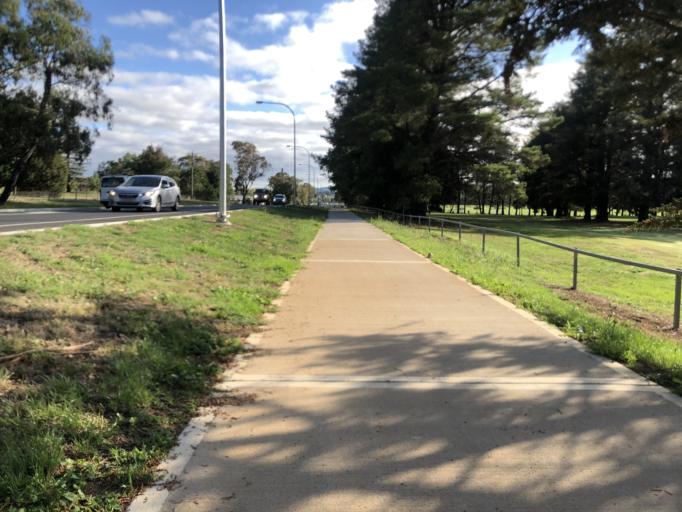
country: AU
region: New South Wales
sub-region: Orange Municipality
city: Orange
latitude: -33.3111
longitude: 149.0954
